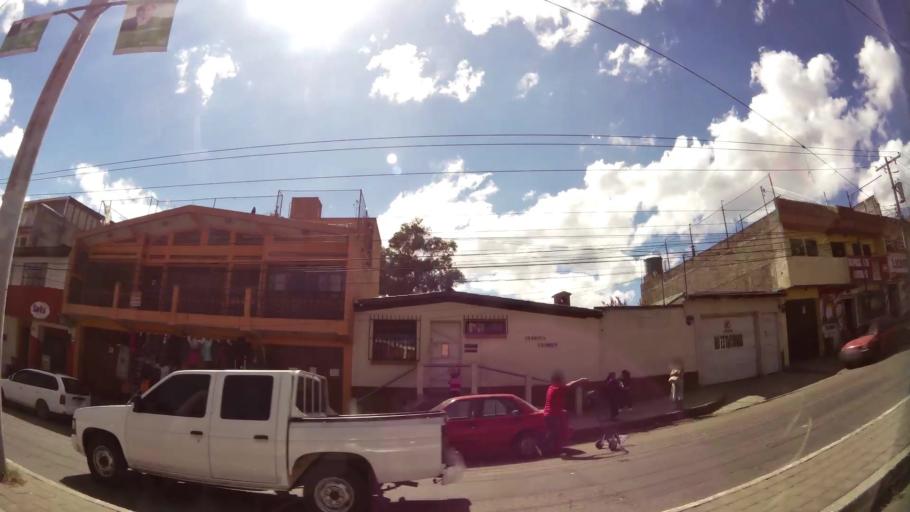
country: GT
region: Quetzaltenango
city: Quetzaltenango
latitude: 14.8452
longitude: -91.5327
